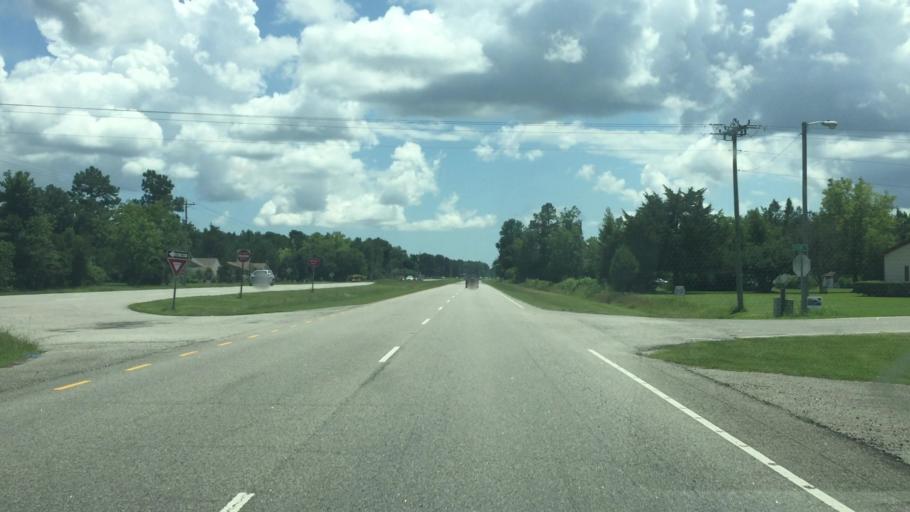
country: US
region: South Carolina
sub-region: Horry County
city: Loris
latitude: 33.9940
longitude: -78.7504
